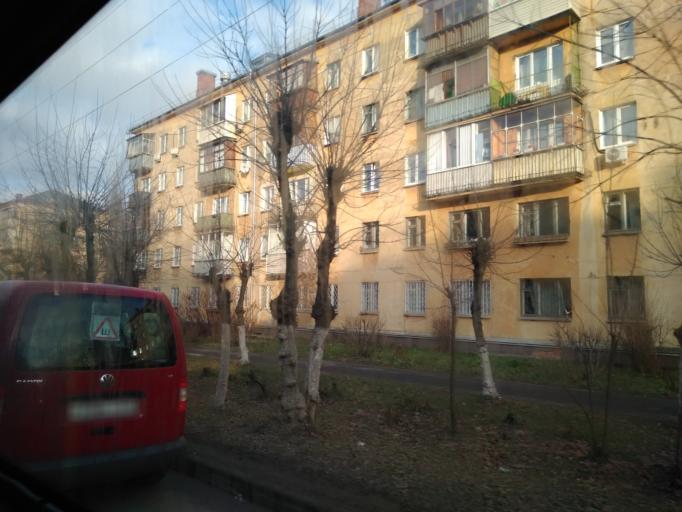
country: RU
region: Moskovskaya
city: Zhukovskiy
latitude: 55.5995
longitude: 38.1231
